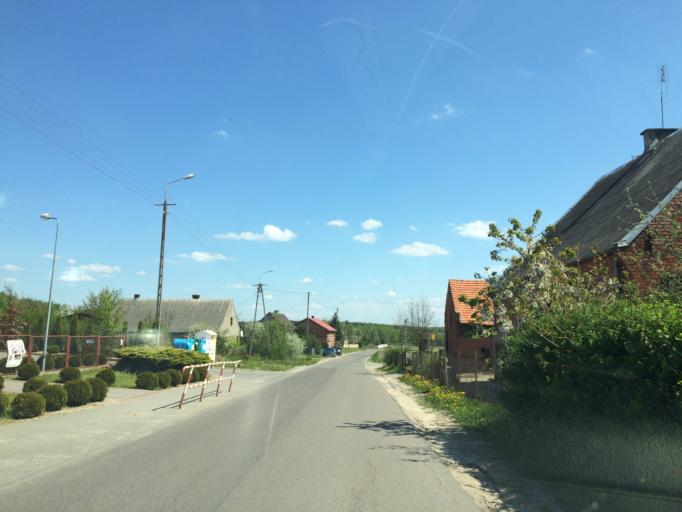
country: PL
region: Warmian-Masurian Voivodeship
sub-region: Powiat nowomiejski
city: Kurzetnik
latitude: 53.3850
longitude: 19.4695
